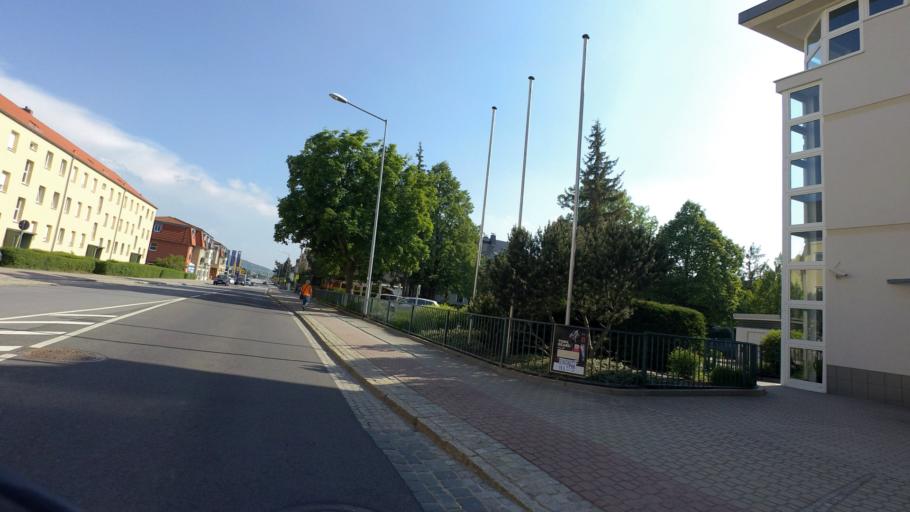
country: DE
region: Saxony
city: Bautzen
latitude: 51.1715
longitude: 14.4241
